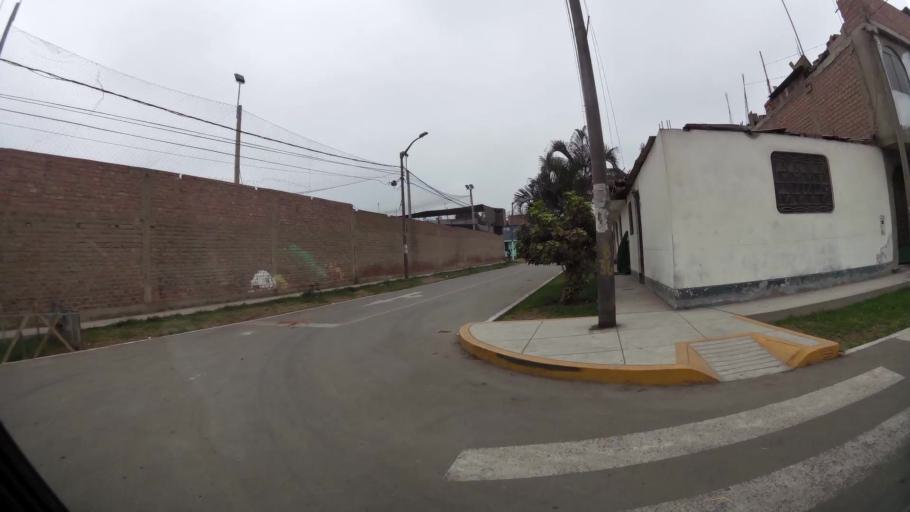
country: PE
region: Lima
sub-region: Lima
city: Urb. Santo Domingo
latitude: -11.8926
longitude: -77.0667
